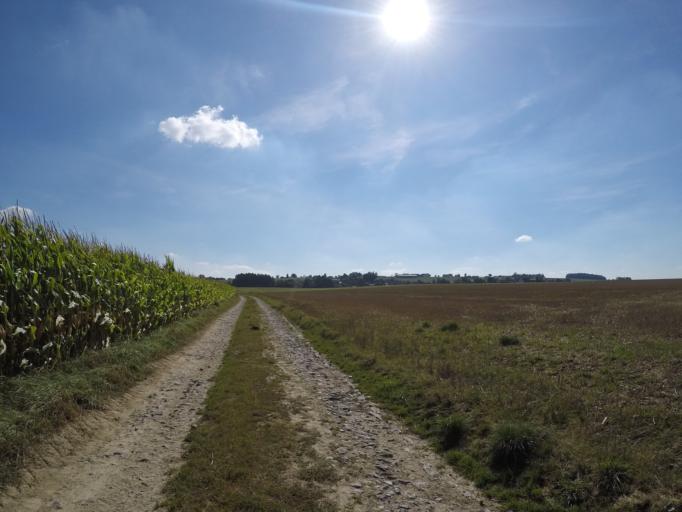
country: BE
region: Wallonia
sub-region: Province de Namur
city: Ciney
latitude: 50.3183
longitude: 5.0557
